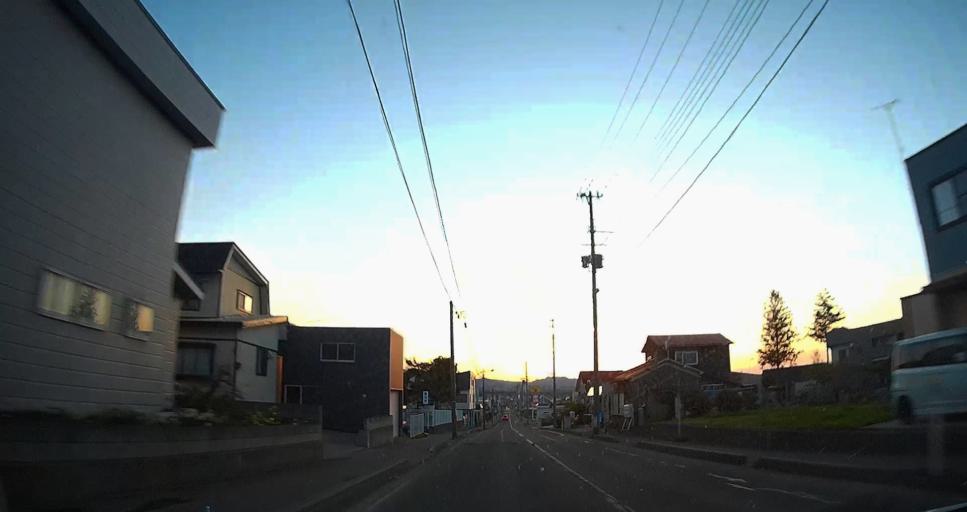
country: JP
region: Aomori
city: Misawa
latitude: 40.8686
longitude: 141.1204
